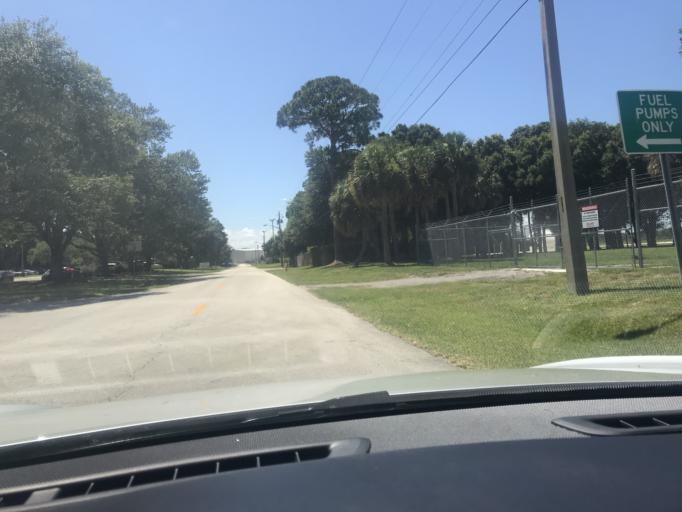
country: US
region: Florida
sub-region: Indian River County
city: Gifford
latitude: 27.6543
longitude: -80.4271
